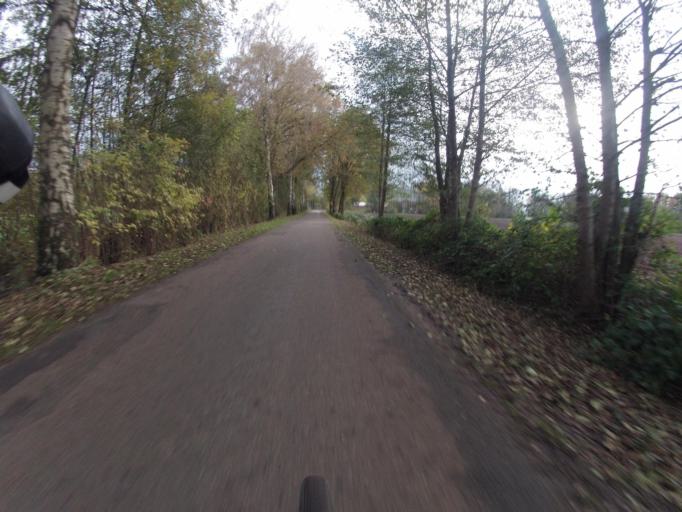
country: DE
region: North Rhine-Westphalia
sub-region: Regierungsbezirk Munster
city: Horstel
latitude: 52.2621
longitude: 7.5690
